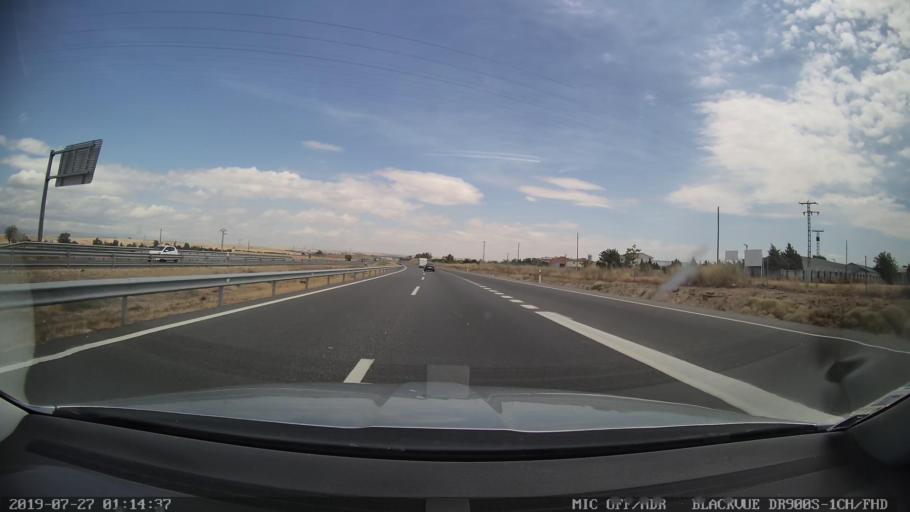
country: ES
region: Castille-La Mancha
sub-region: Province of Toledo
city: Santa Olalla
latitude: 40.0375
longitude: -4.4094
